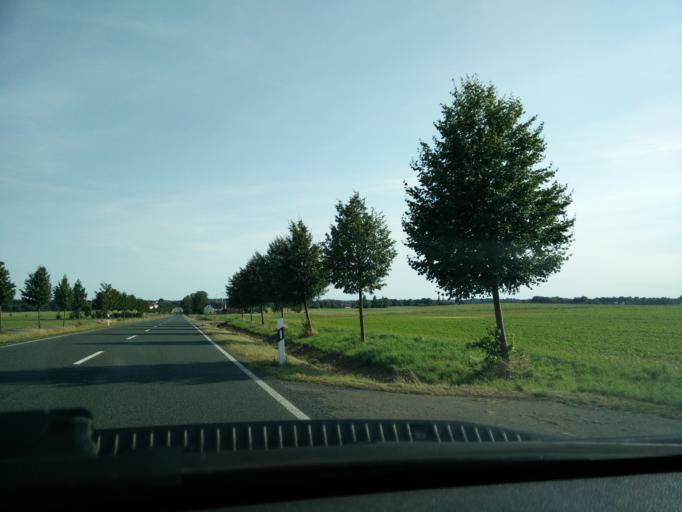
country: DE
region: Saxony
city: Bad Lausick
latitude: 51.1635
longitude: 12.6283
